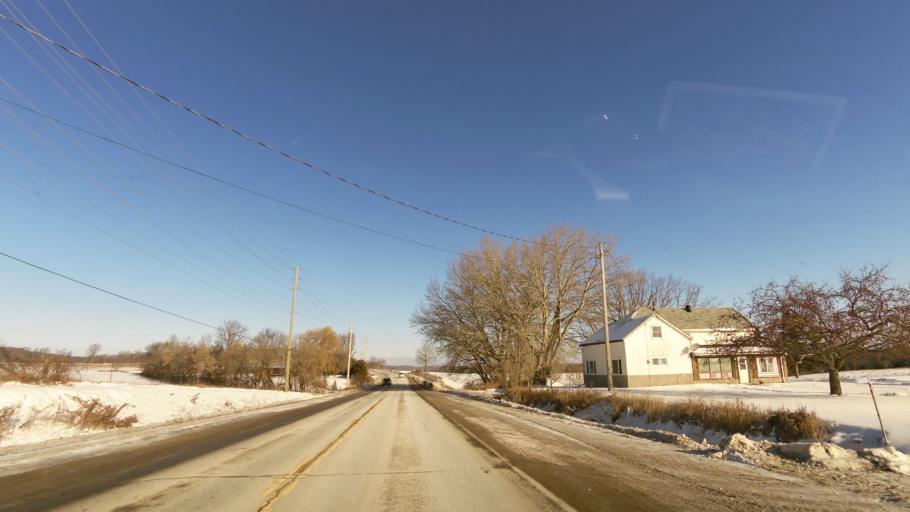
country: CA
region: Ontario
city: Quinte West
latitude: 44.2317
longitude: -77.8215
